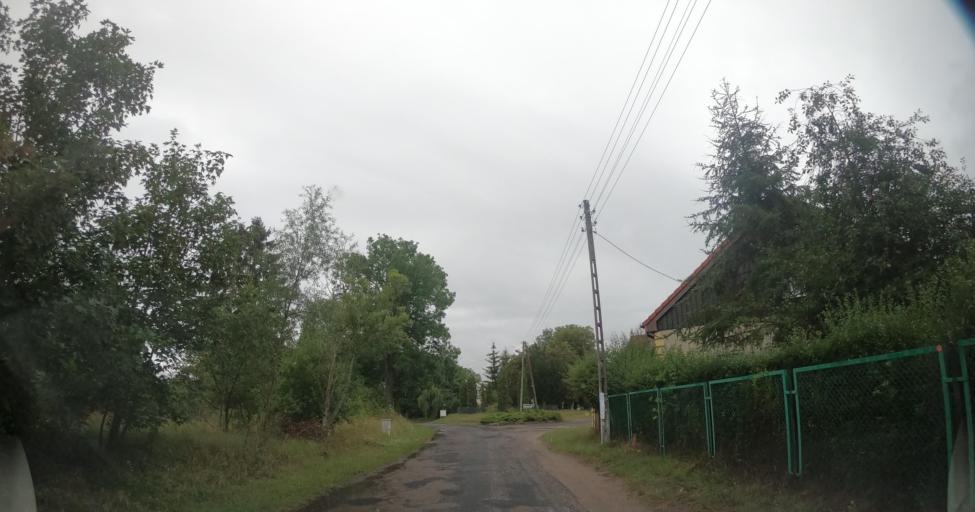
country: PL
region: West Pomeranian Voivodeship
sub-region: Powiat lobeski
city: Wegorzyno
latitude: 53.5250
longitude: 15.4963
